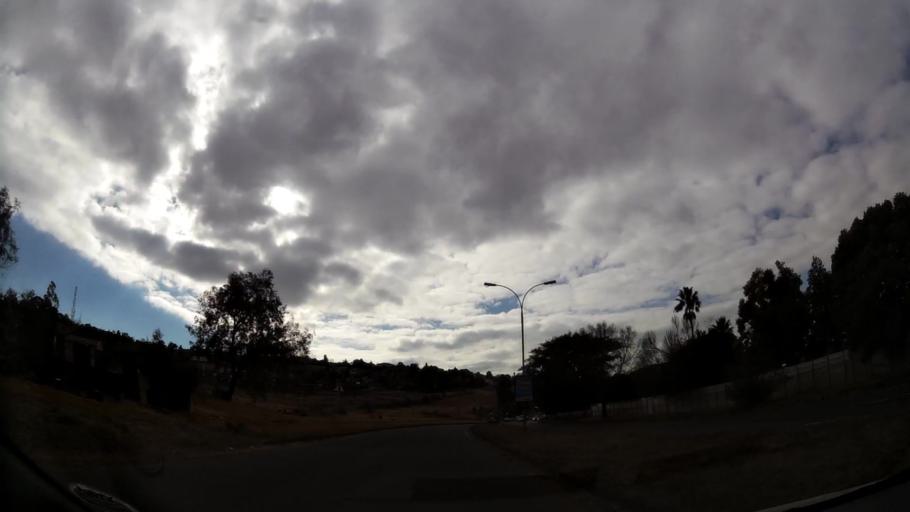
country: ZA
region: Gauteng
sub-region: City of Johannesburg Metropolitan Municipality
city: Roodepoort
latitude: -26.1079
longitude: 27.8573
